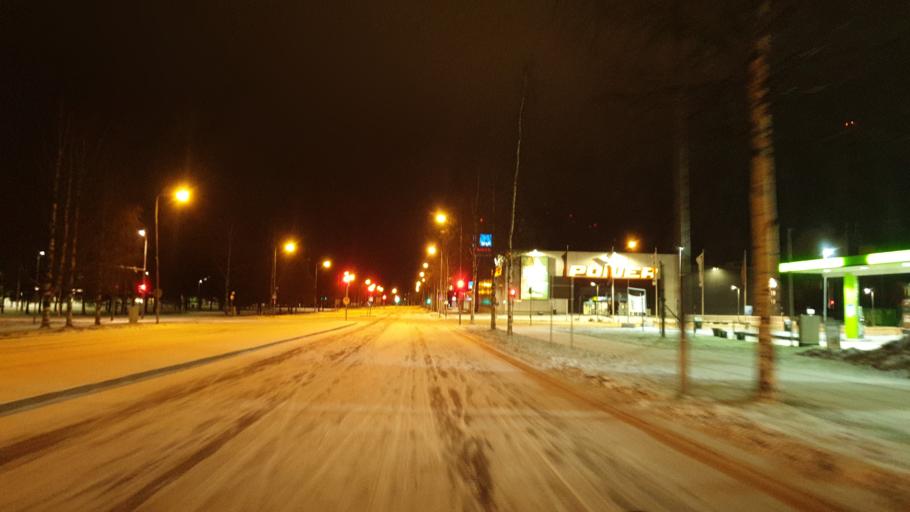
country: FI
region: Northern Ostrobothnia
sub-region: Oulu
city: Oulu
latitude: 64.9965
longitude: 25.4634
